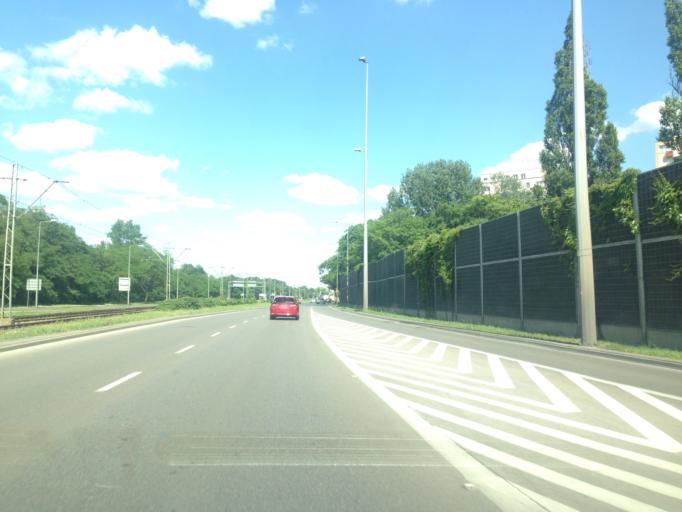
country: PL
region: Masovian Voivodeship
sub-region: Warszawa
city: Praga Polnoc
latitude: 52.2650
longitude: 21.0252
